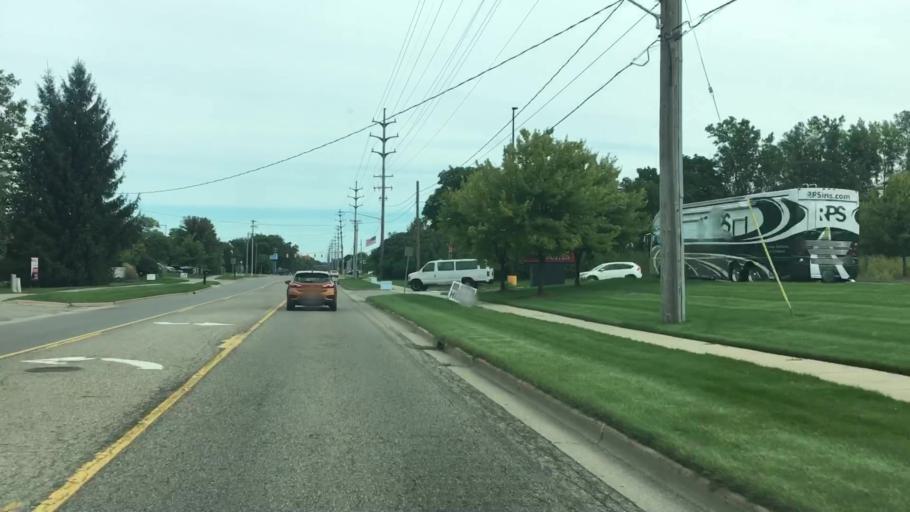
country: US
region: Michigan
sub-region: Ottawa County
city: Jenison
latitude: 42.8828
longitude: -85.7822
